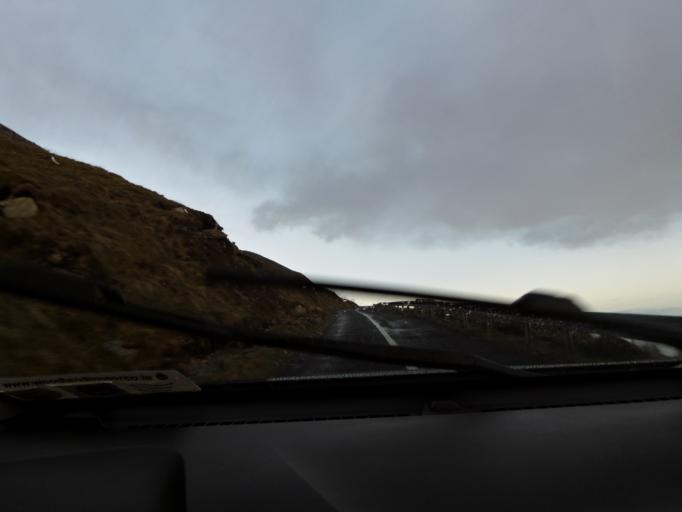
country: IE
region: Connaught
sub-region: Maigh Eo
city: Belmullet
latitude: 53.9705
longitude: -10.1842
